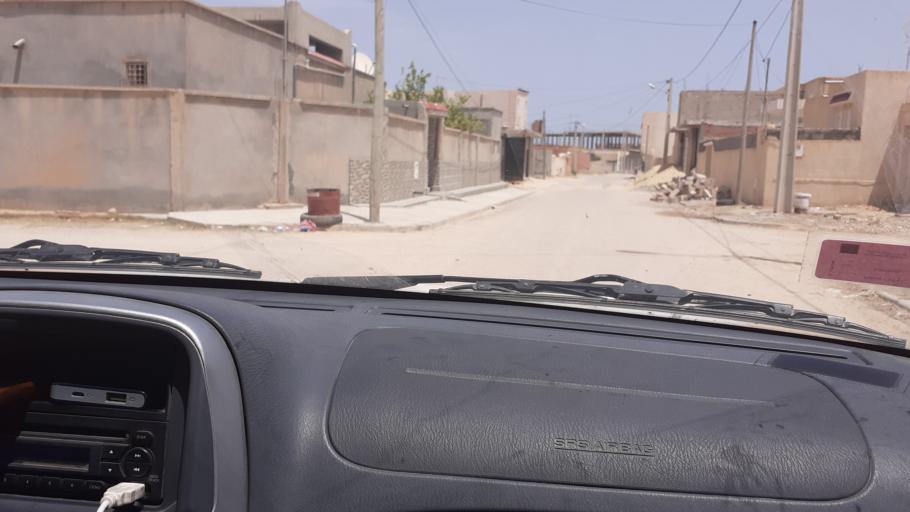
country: TN
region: Qabis
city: Matmata
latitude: 33.6116
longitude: 10.2905
